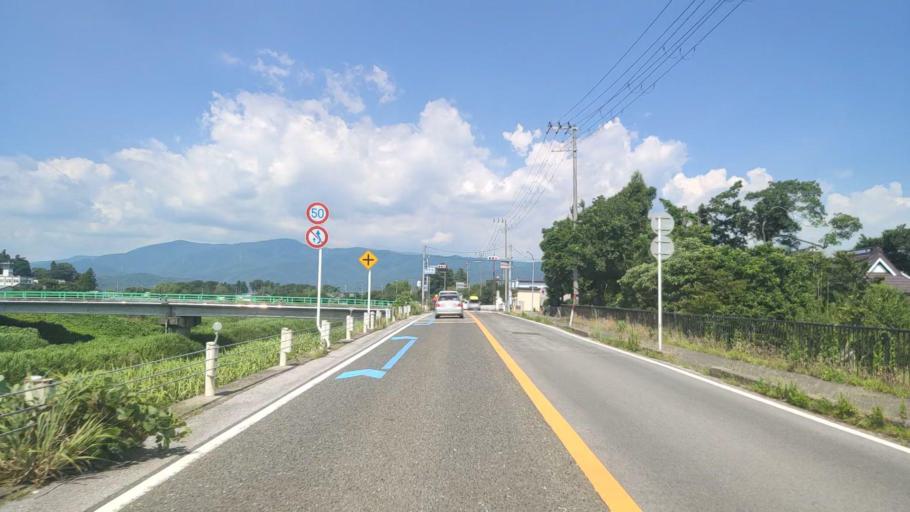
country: JP
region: Shiga Prefecture
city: Nagahama
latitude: 35.4678
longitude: 136.2079
